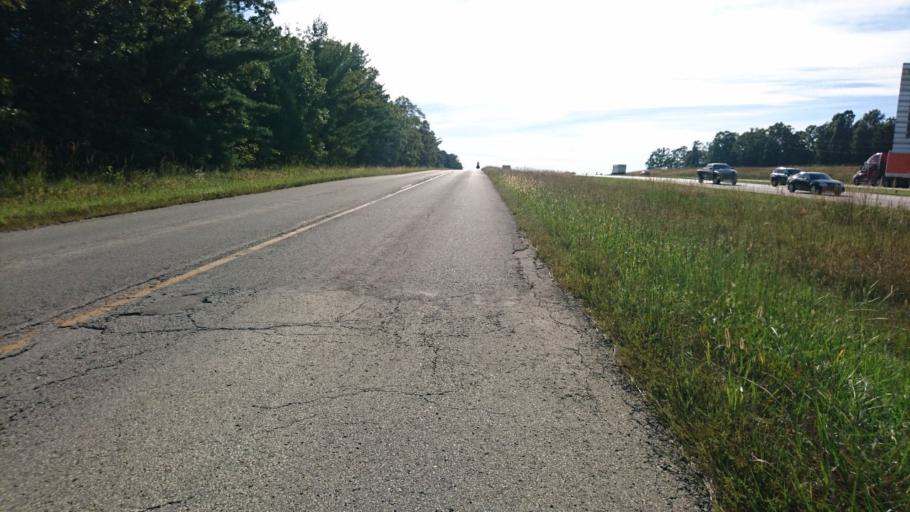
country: US
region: Missouri
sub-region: Crawford County
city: Bourbon
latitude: 38.1160
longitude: -91.3224
